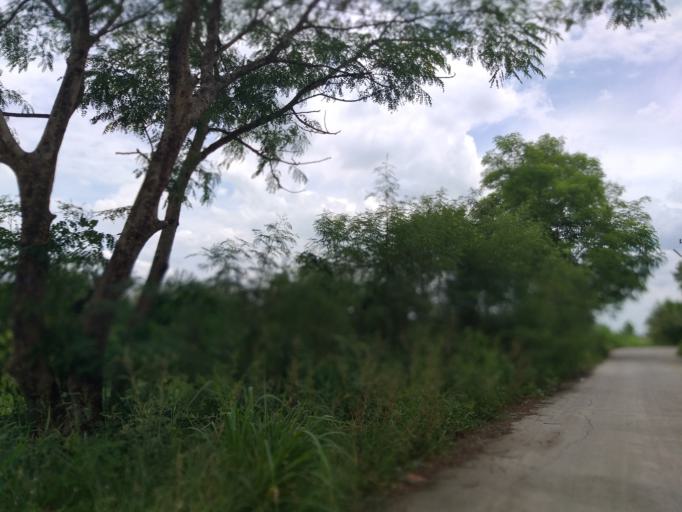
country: TH
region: Pathum Thani
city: Ban Lam Luk Ka
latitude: 14.0097
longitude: 100.8656
